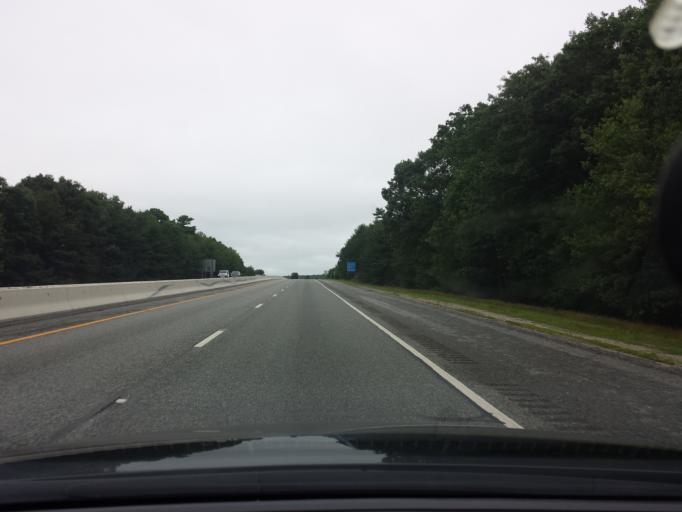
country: US
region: Rhode Island
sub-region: Washington County
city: Hope Valley
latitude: 41.5175
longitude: -71.6890
